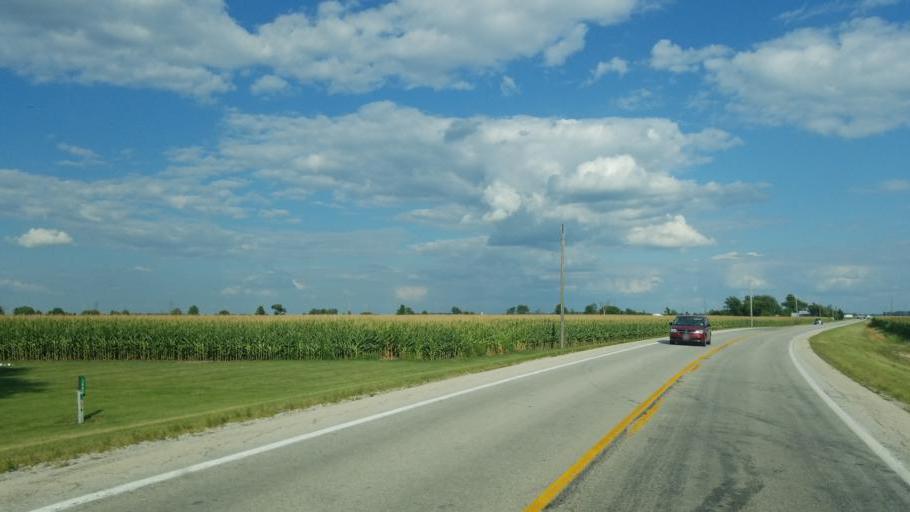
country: US
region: Ohio
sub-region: Wood County
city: Pemberville
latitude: 41.3552
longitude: -83.4721
